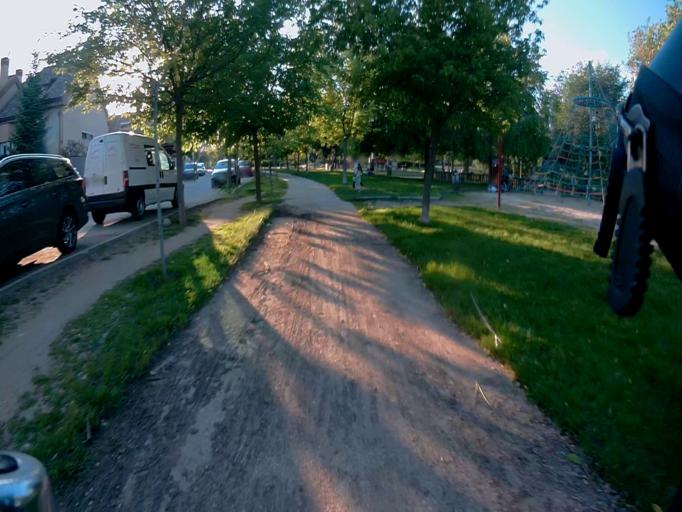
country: ES
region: Madrid
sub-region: Provincia de Madrid
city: Fuenlabrada
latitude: 40.3134
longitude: -3.7918
